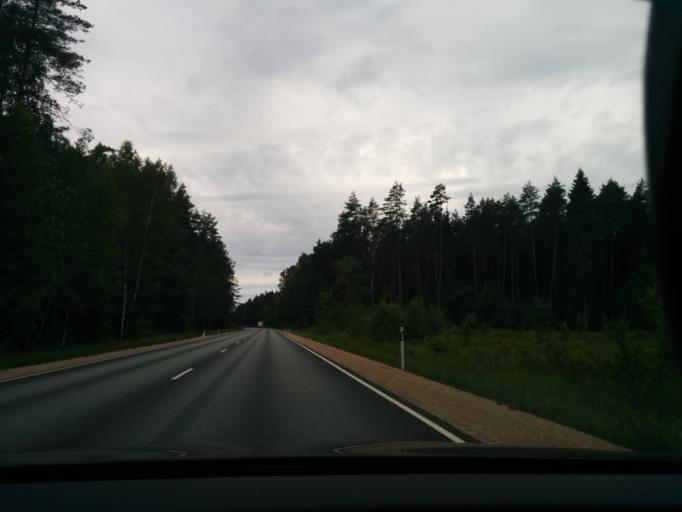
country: LV
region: Ikskile
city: Ikskile
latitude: 56.8736
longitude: 24.5342
